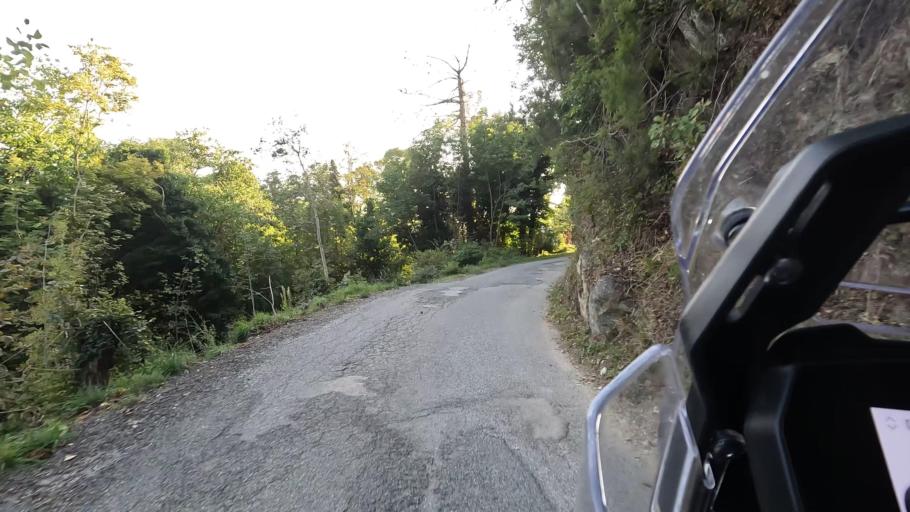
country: IT
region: Liguria
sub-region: Provincia di Savona
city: San Giovanni
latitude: 44.3941
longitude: 8.5213
